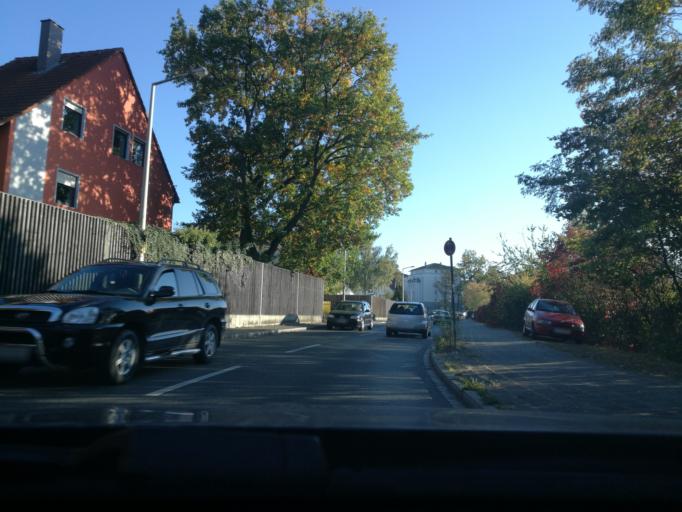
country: DE
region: Bavaria
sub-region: Regierungsbezirk Mittelfranken
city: Nuernberg
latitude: 49.4766
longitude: 11.1211
